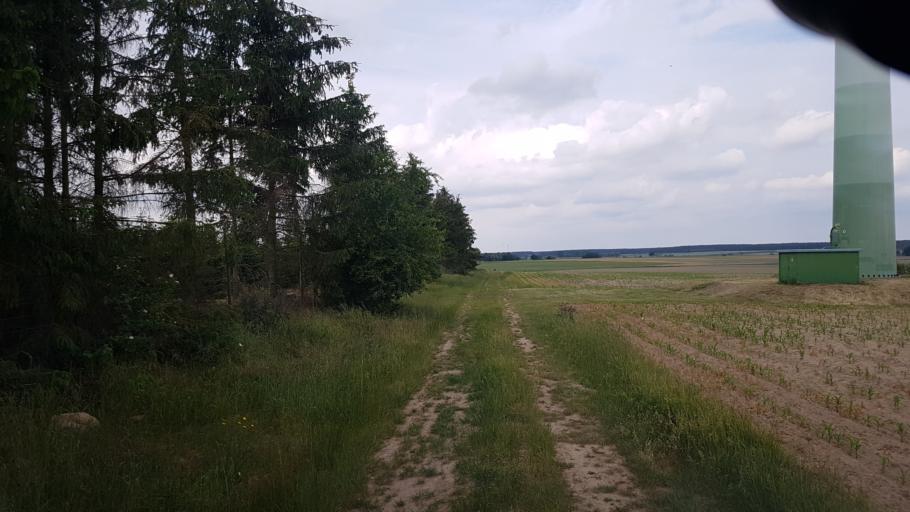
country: DE
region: Brandenburg
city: Dahme
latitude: 51.8800
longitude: 13.4041
